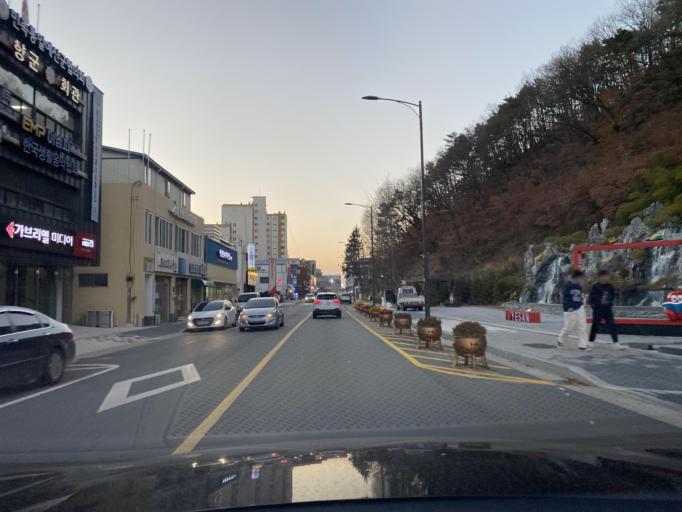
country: KR
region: Chungcheongnam-do
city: Yesan
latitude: 36.6787
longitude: 126.8398
